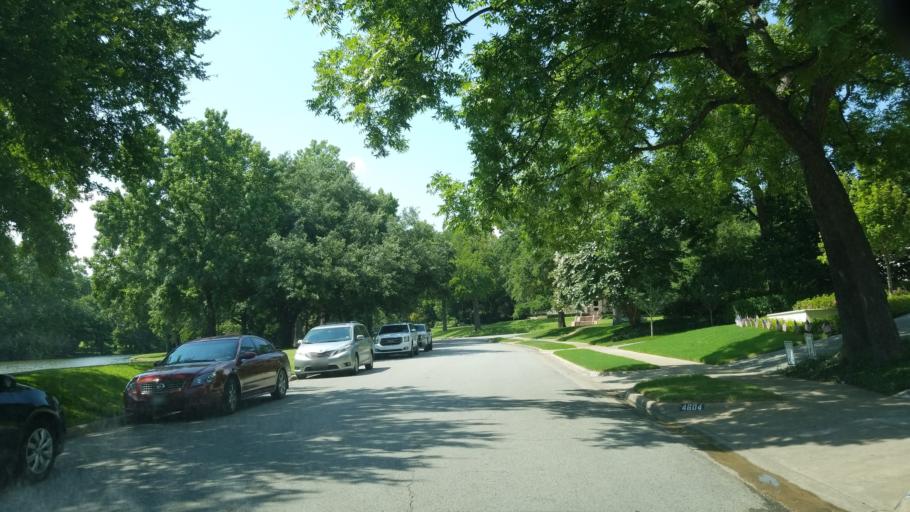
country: US
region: Texas
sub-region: Dallas County
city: Highland Park
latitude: 32.8272
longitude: -96.8010
